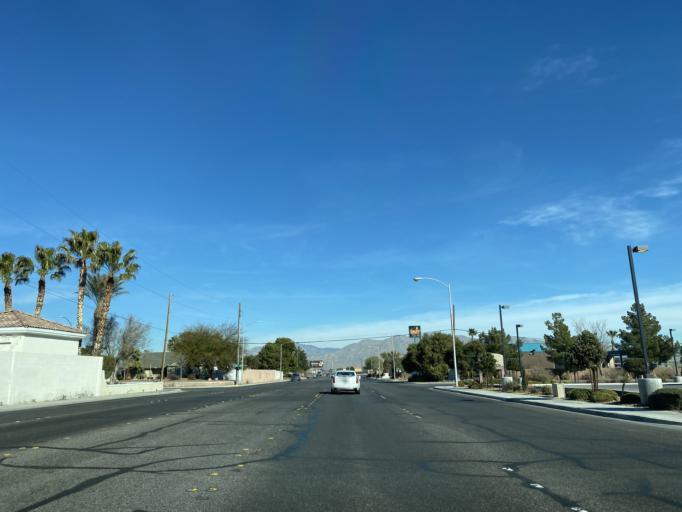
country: US
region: Nevada
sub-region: Clark County
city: Las Vegas
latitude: 36.2274
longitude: -115.2256
